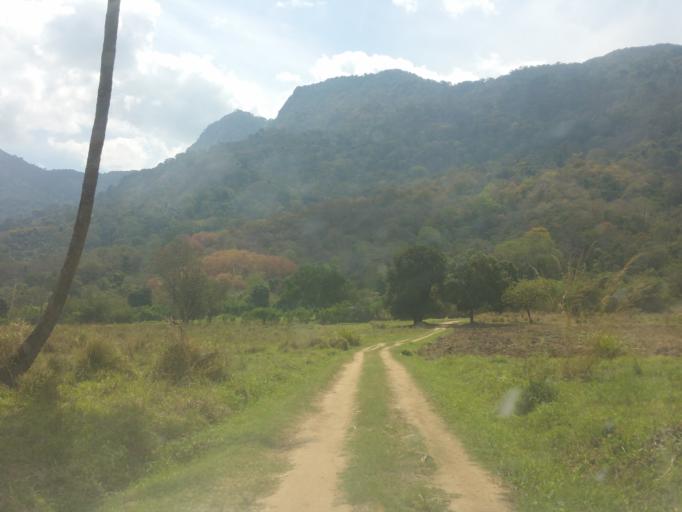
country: TZ
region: Morogoro
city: Kidatu
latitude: -7.8356
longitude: 36.8923
